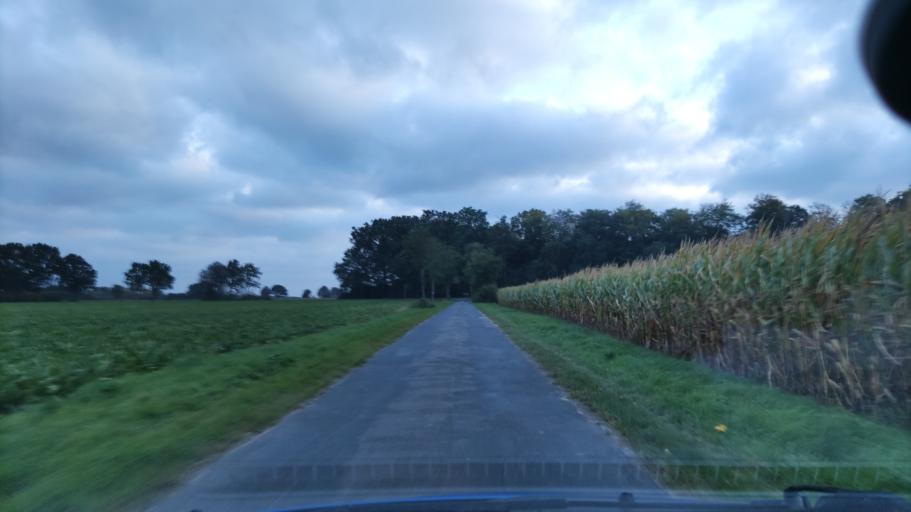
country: DE
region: Lower Saxony
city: Tosterglope
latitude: 53.2248
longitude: 10.8273
